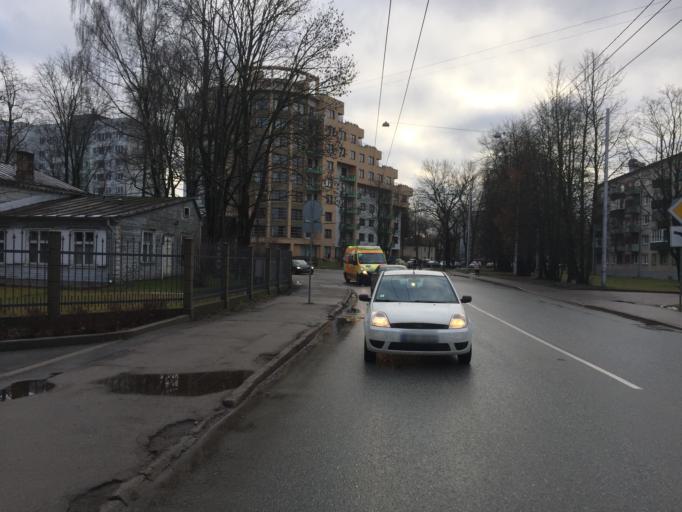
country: LV
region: Marupe
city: Marupe
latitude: 56.9493
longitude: 24.0547
